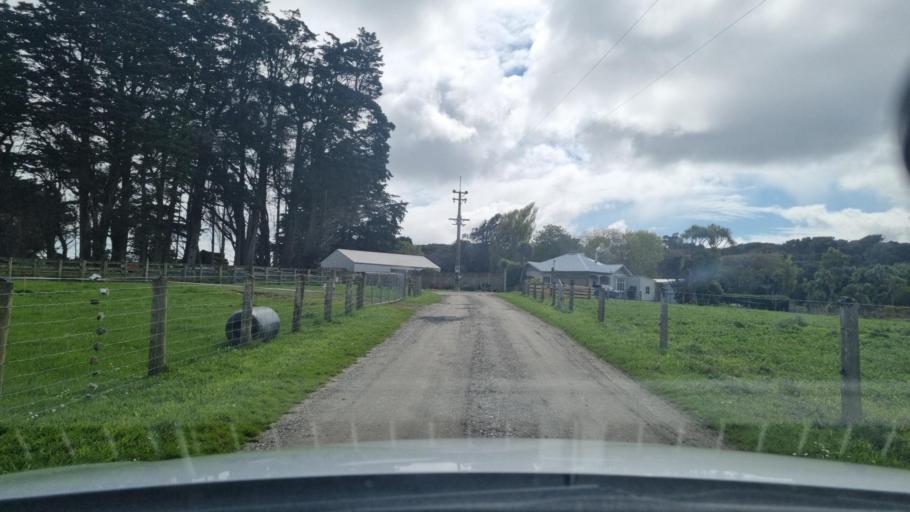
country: NZ
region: Southland
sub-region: Invercargill City
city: Bluff
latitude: -46.5254
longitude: 168.2982
